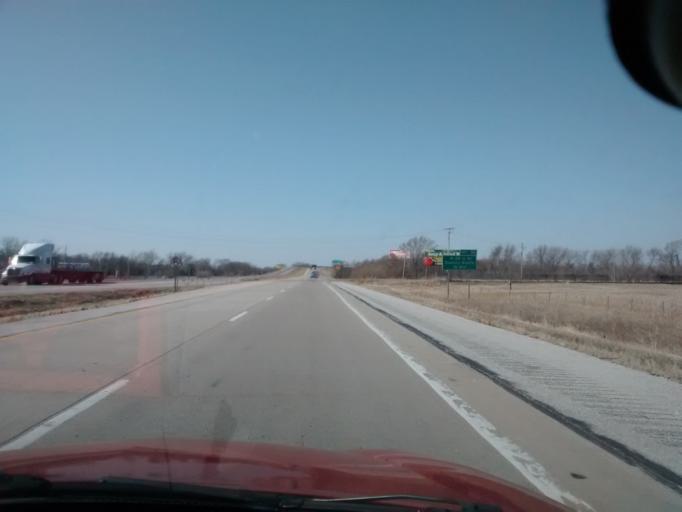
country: US
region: Iowa
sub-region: Pottawattamie County
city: Council Bluffs
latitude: 41.2815
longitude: -95.8716
